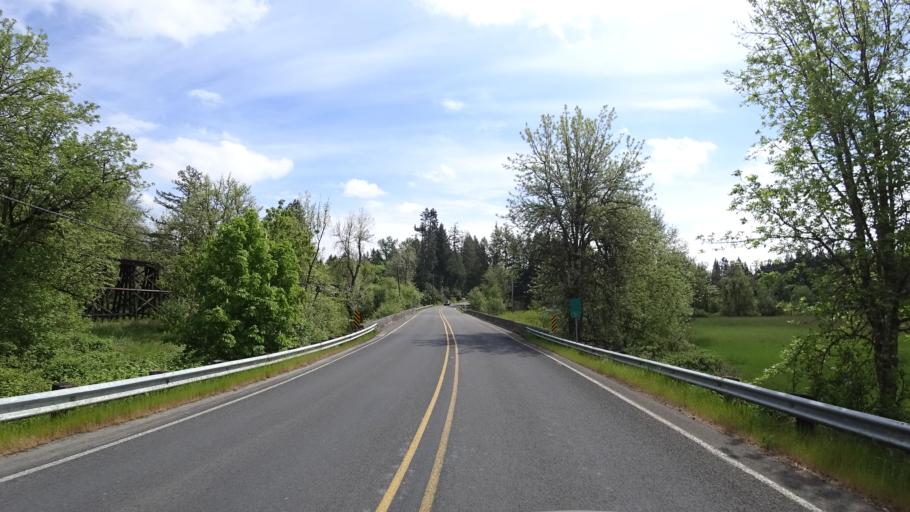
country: US
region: Oregon
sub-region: Washington County
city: Hillsboro
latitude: 45.5428
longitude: -123.0045
